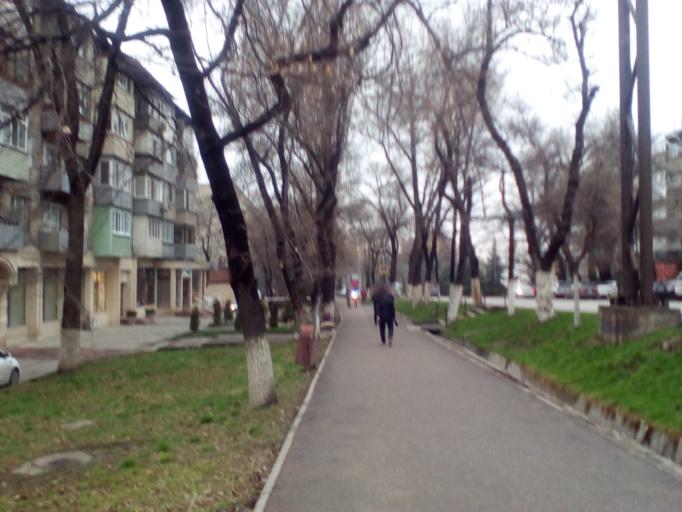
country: KZ
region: Almaty Qalasy
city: Almaty
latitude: 43.2229
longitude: 76.9626
